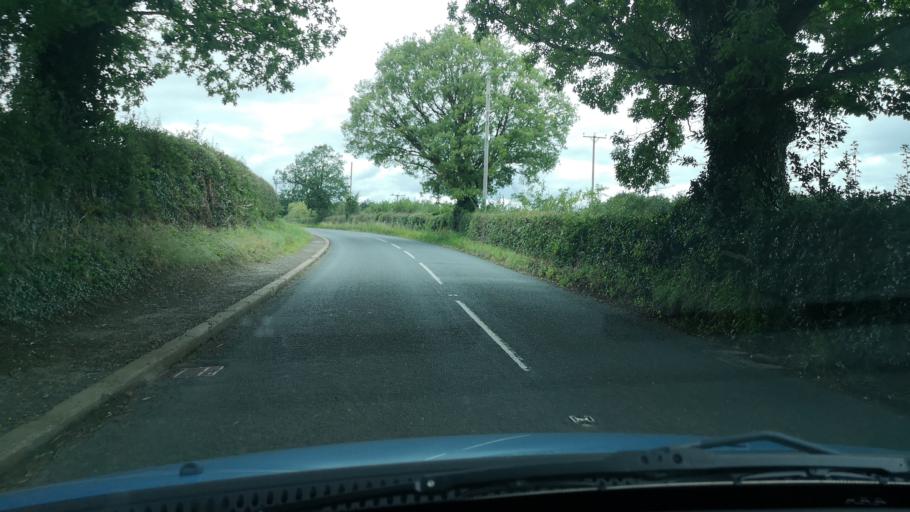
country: GB
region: England
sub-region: City and Borough of Wakefield
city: Crigglestone
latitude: 53.6318
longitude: -1.5496
